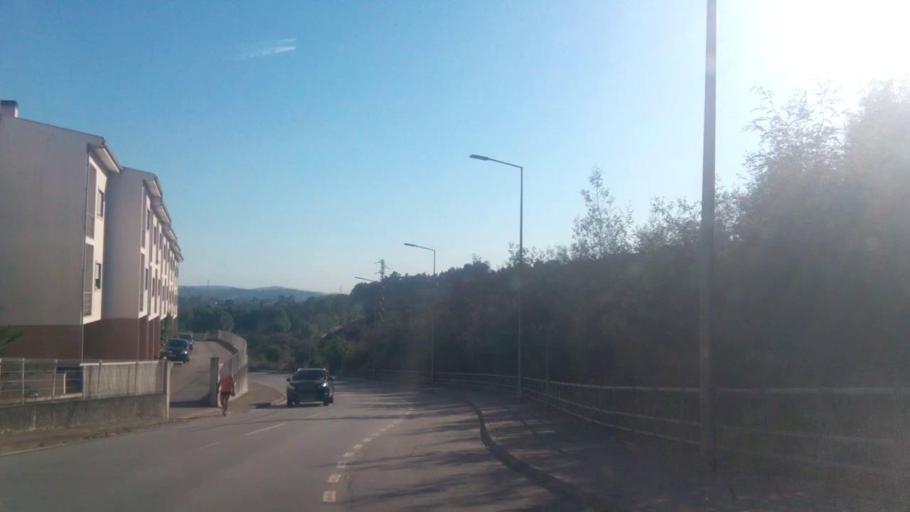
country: PT
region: Porto
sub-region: Penafiel
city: Penafiel
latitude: 41.1987
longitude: -8.2831
